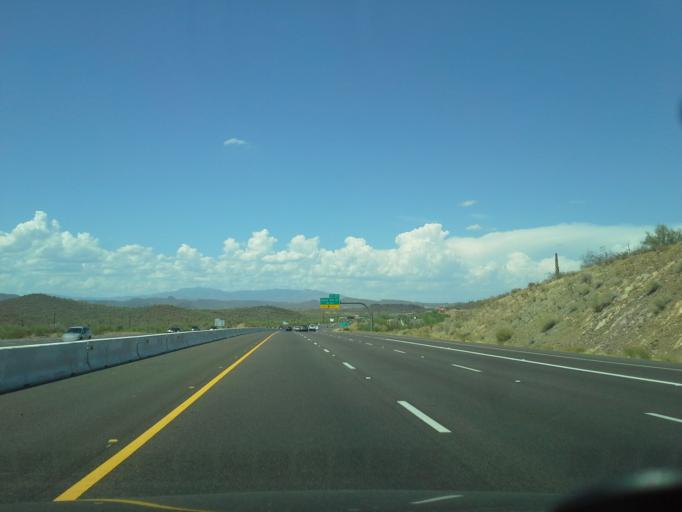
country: US
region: Arizona
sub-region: Maricopa County
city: Anthem
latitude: 33.8237
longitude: -112.1427
